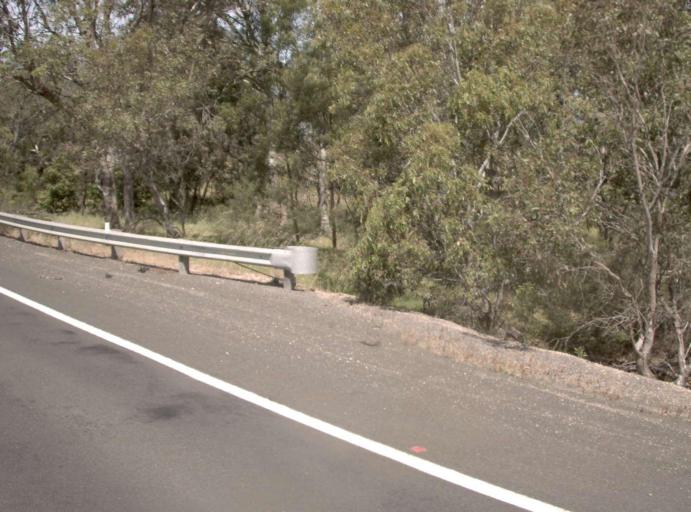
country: AU
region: Victoria
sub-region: East Gippsland
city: Bairnsdale
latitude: -37.8828
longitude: 147.4144
